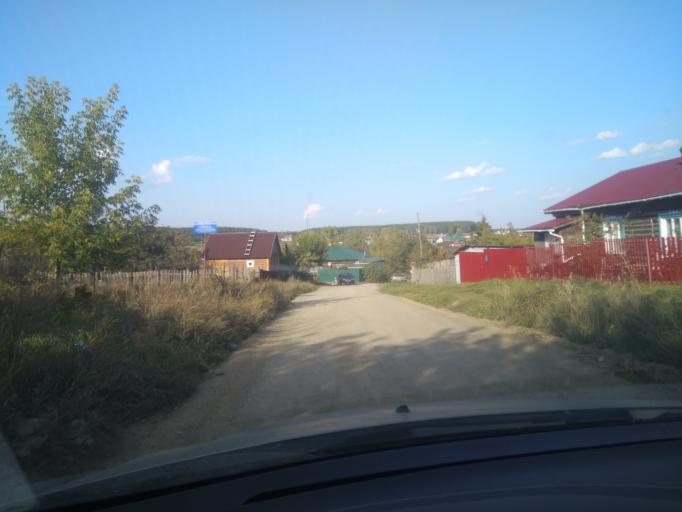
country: RU
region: Sverdlovsk
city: Pokrovskoye
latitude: 56.4323
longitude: 61.5938
